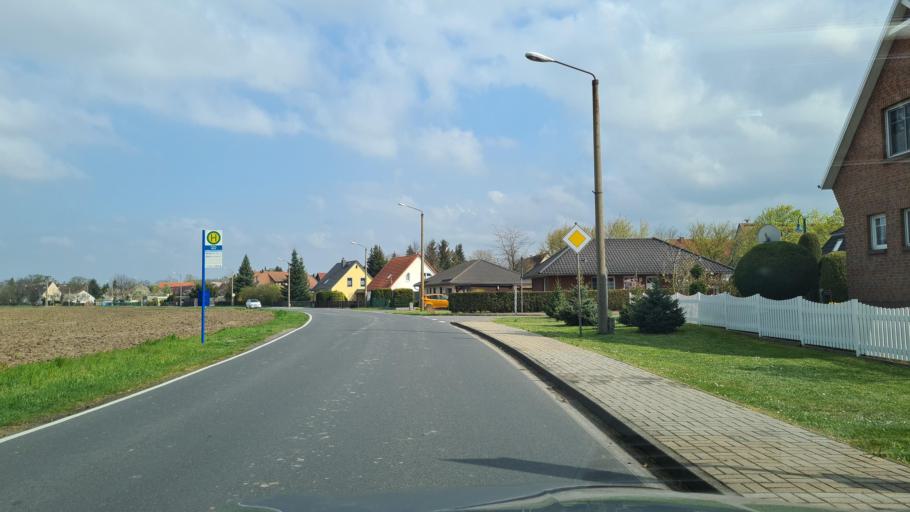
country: DE
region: Saxony
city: Nauwalde
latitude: 51.3898
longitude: 13.4429
